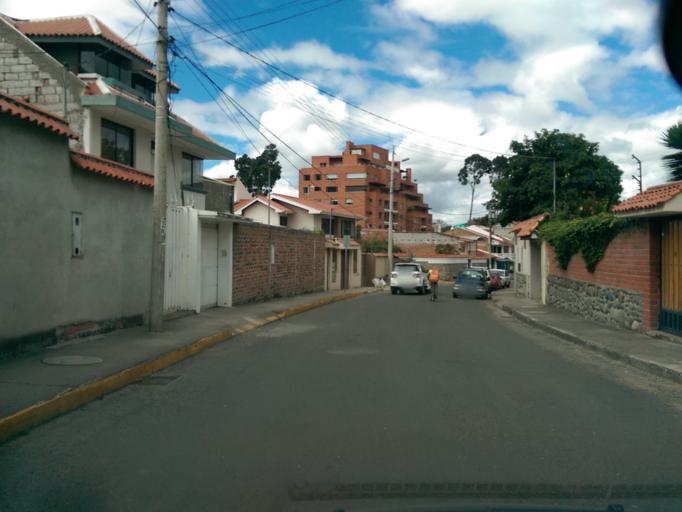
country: EC
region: Azuay
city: Cuenca
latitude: -2.9115
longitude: -79.0129
